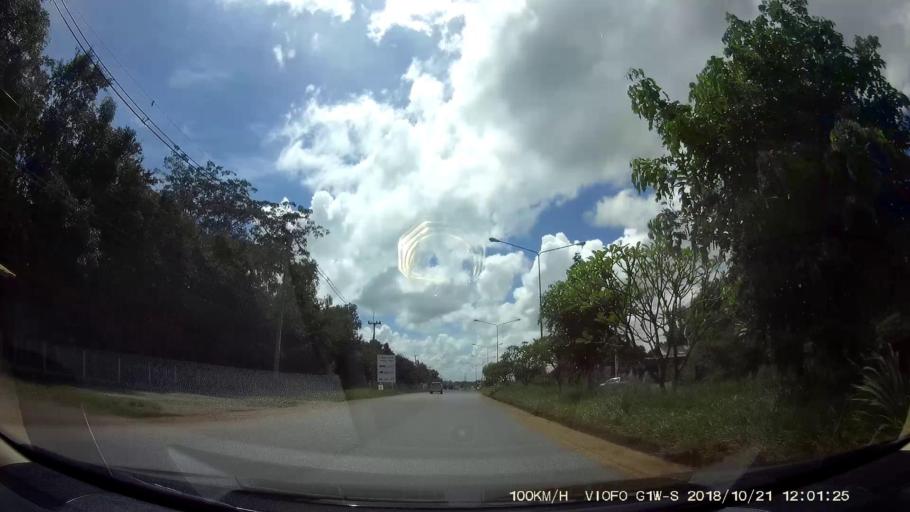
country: TH
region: Chaiyaphum
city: Chatturat
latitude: 15.5386
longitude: 101.8356
